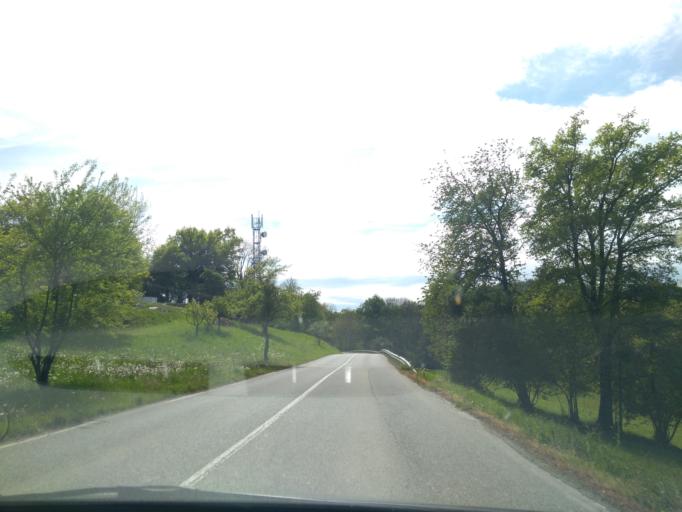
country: FR
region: Rhone-Alpes
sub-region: Departement de la Haute-Savoie
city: Marcellaz-Albanais
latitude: 45.8743
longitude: 6.0104
